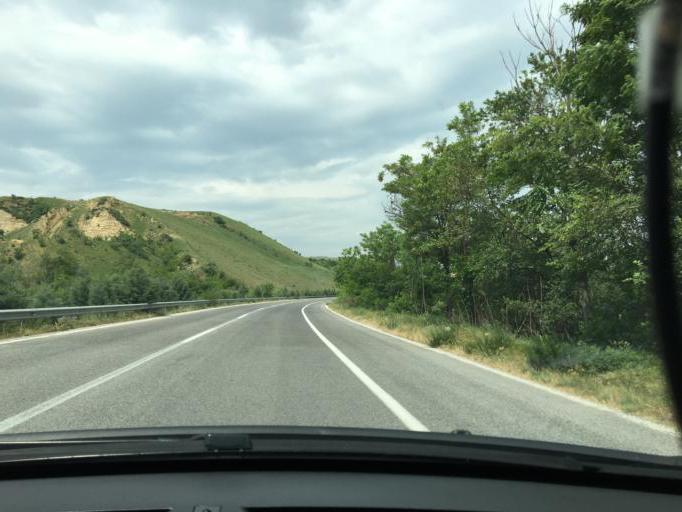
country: MK
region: Demir Kapija
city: Demir Kapija
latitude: 41.4177
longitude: 22.1966
